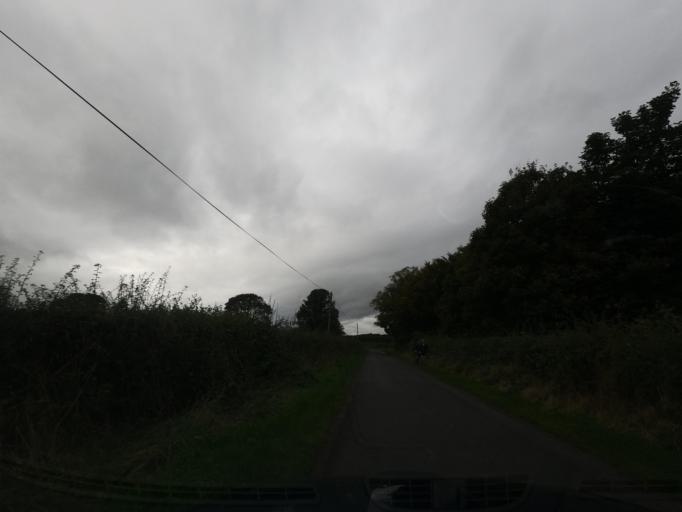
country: GB
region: England
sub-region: Northumberland
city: Doddington
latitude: 55.6001
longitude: -2.0306
